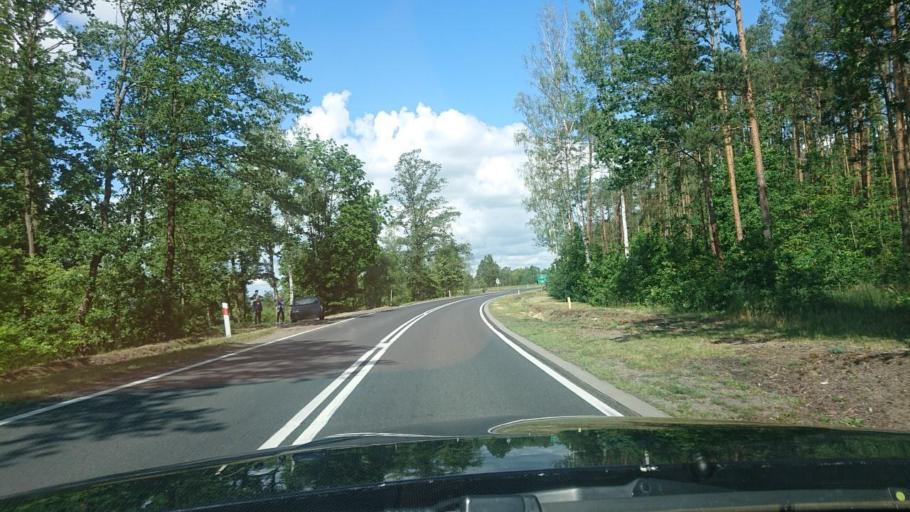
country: PL
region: Lubusz
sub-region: Powiat zaganski
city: Szprotawa
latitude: 51.5470
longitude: 15.5979
